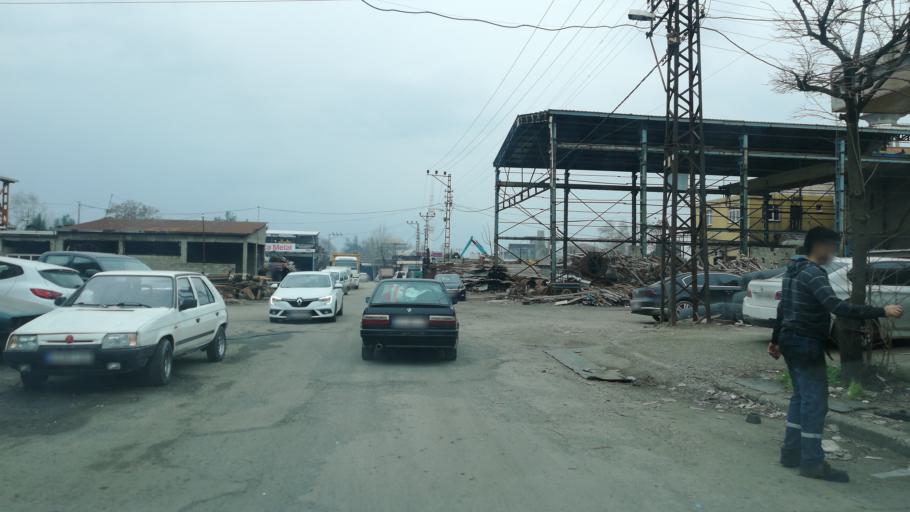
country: TR
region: Kahramanmaras
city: Kahramanmaras
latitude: 37.5668
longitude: 36.9565
